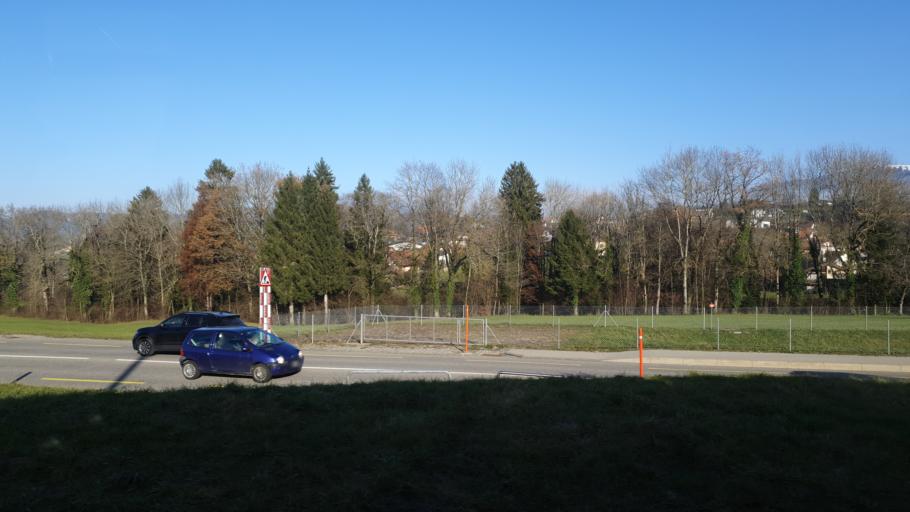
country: CH
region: Fribourg
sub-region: Veveyse District
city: Attalens
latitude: 46.5226
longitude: 6.8650
